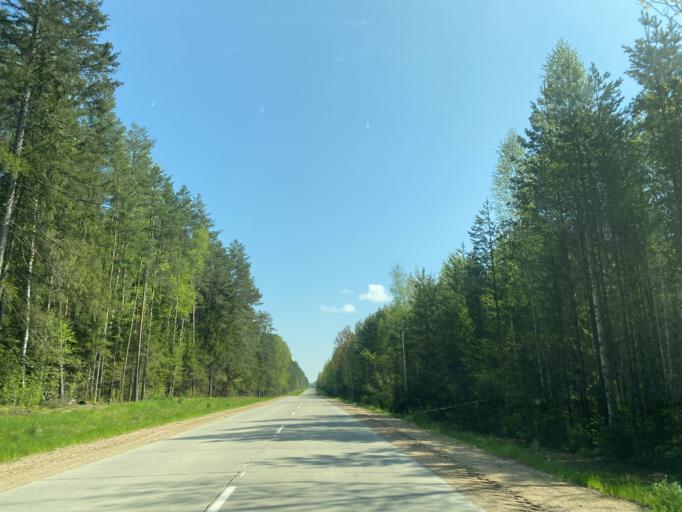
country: BY
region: Minsk
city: Horad Barysaw
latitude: 54.1684
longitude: 28.5121
